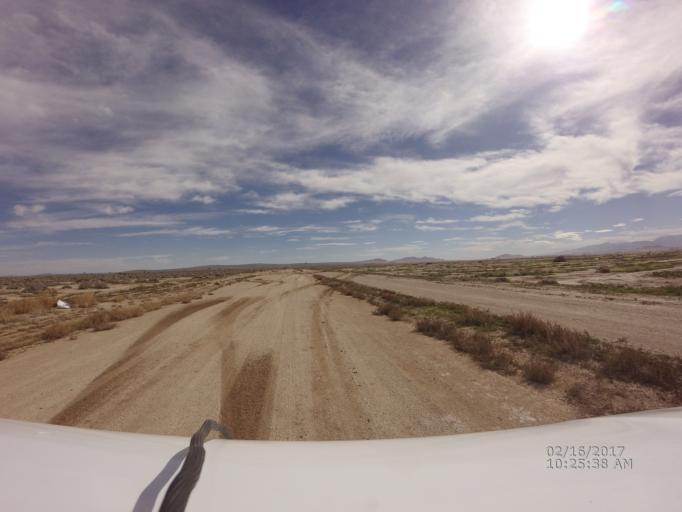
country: US
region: California
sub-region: Los Angeles County
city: Lake Los Angeles
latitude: 34.7342
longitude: -117.9540
